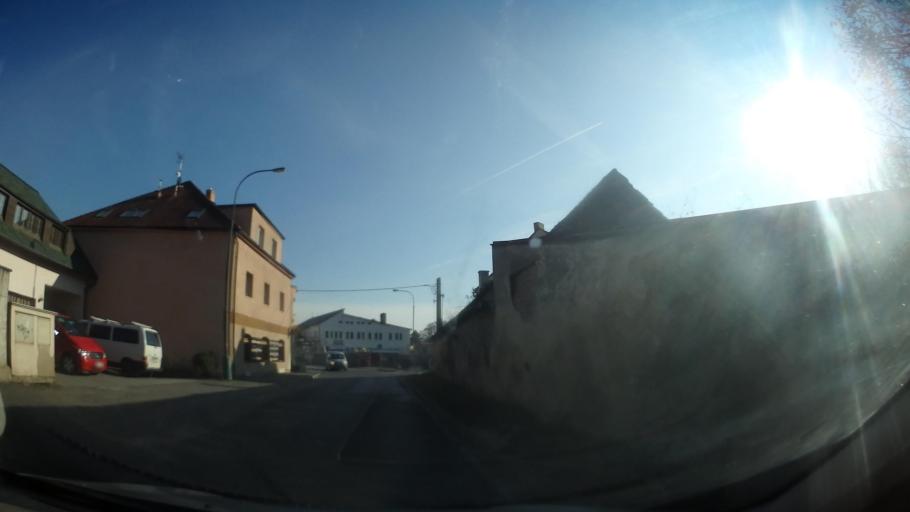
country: CZ
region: Central Bohemia
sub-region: Okres Praha-Vychod
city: Mnichovice
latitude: 49.9369
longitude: 14.7073
